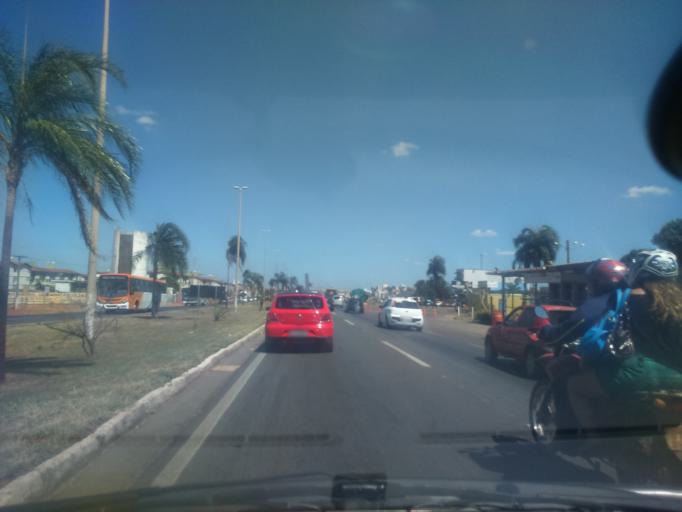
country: BR
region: Goias
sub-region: Luziania
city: Luziania
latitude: -16.0672
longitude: -47.9843
